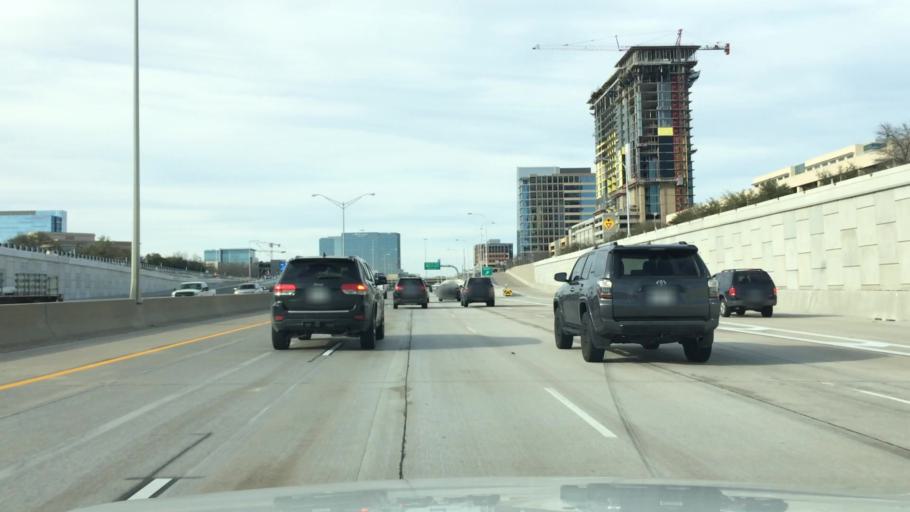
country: US
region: Texas
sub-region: Denton County
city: The Colony
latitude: 33.0730
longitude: -96.8245
